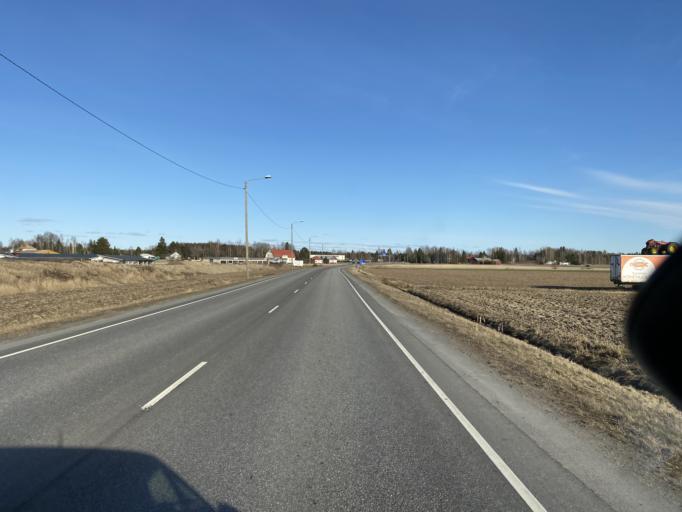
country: FI
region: Satakunta
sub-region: Pori
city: Huittinen
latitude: 61.1676
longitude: 22.6957
